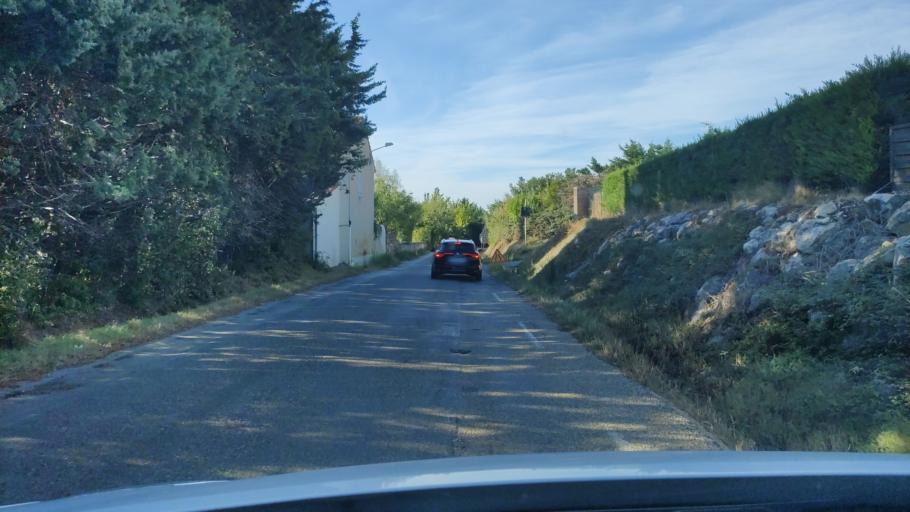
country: FR
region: Languedoc-Roussillon
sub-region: Departement du Gard
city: Saze
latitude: 43.9352
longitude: 4.6520
